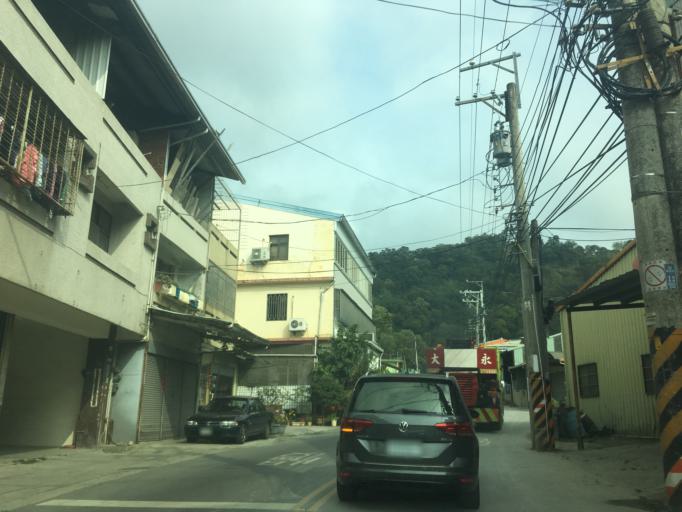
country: TW
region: Taiwan
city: Fengyuan
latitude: 24.2361
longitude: 120.7367
